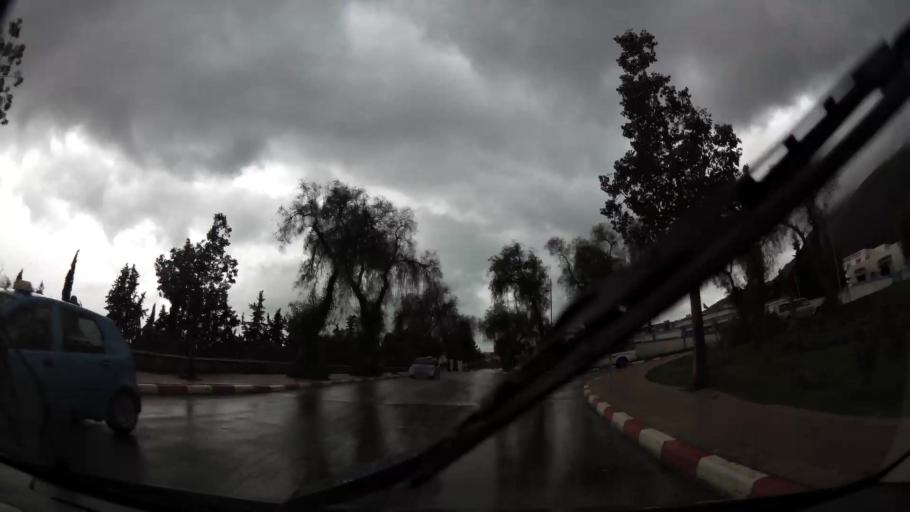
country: MA
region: Tanger-Tetouan
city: Chefchaouene
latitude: 35.1735
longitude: -5.2756
